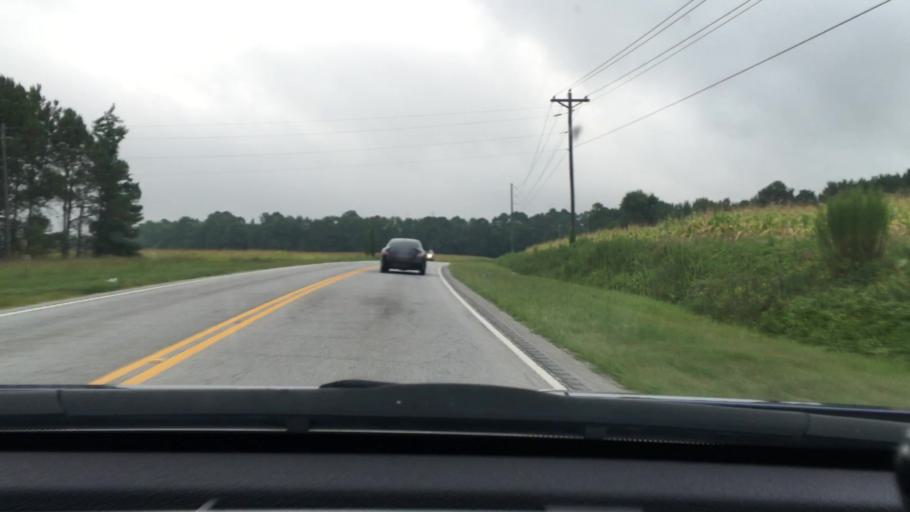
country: US
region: South Carolina
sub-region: Florence County
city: Timmonsville
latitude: 34.1963
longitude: -80.0392
